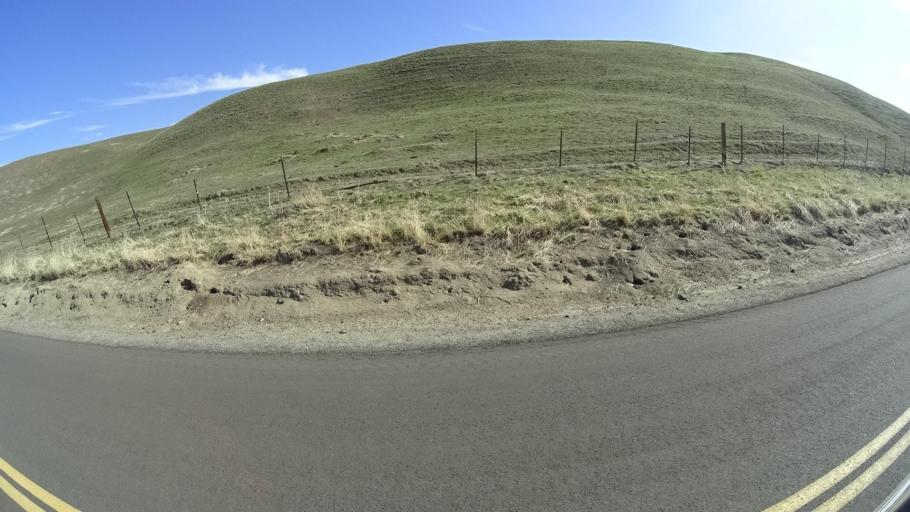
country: US
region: California
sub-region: Tulare County
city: Richgrove
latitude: 35.6487
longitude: -118.9381
